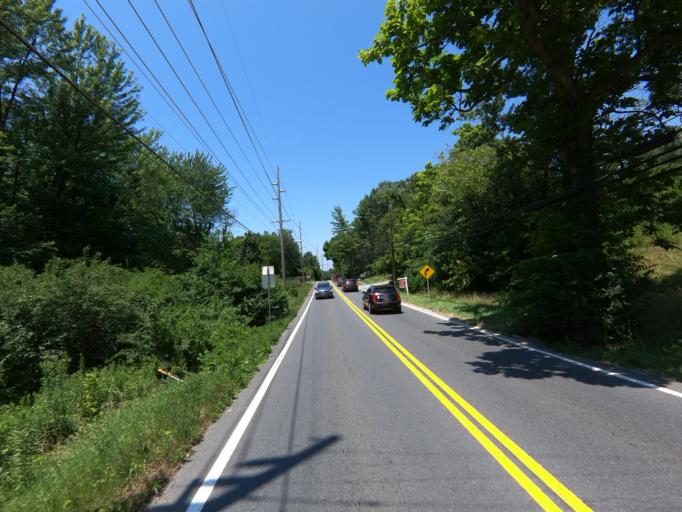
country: US
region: Maryland
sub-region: Montgomery County
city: Clarksburg
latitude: 39.2420
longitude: -77.2838
